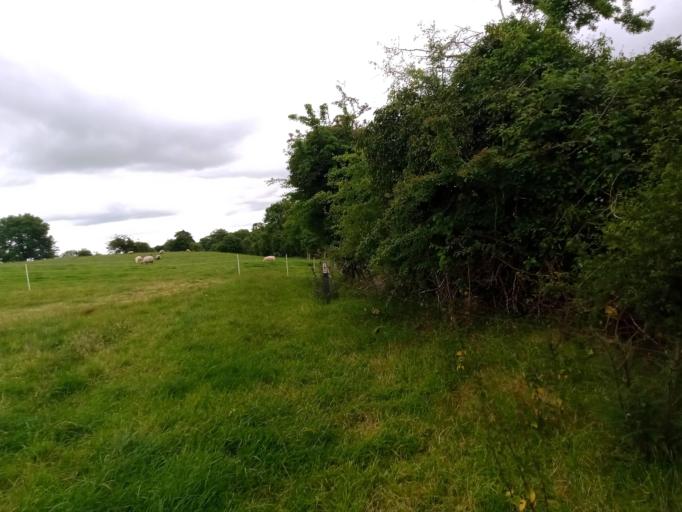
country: IE
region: Leinster
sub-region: Laois
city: Rathdowney
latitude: 52.7806
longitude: -7.4671
